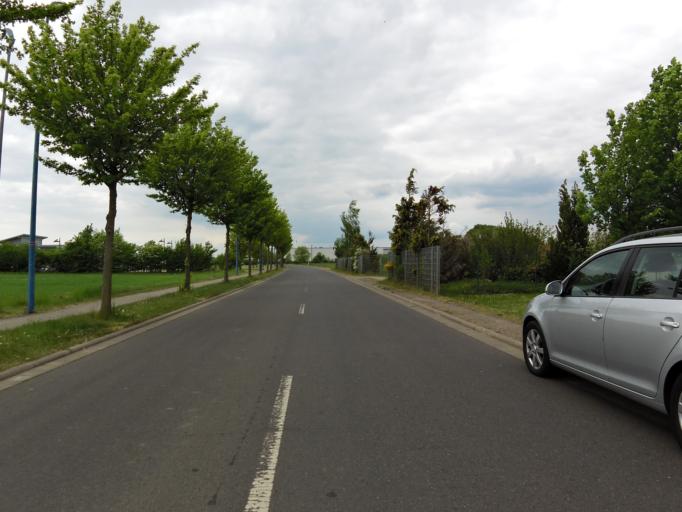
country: DE
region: Thuringia
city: Gotha
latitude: 50.9252
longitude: 10.7132
